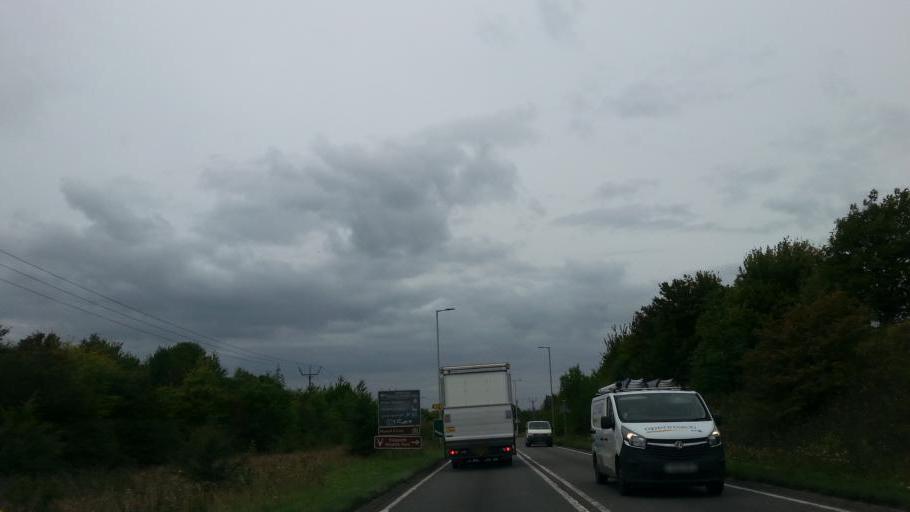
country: GB
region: England
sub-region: Hertfordshire
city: Royston
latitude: 52.0598
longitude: -0.0105
